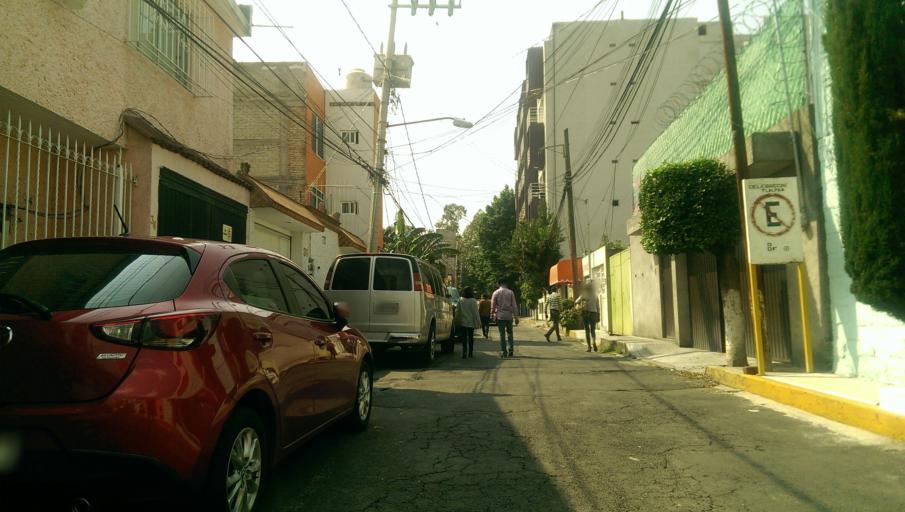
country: MX
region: Mexico City
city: Tlalpan
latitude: 19.2845
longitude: -99.1323
